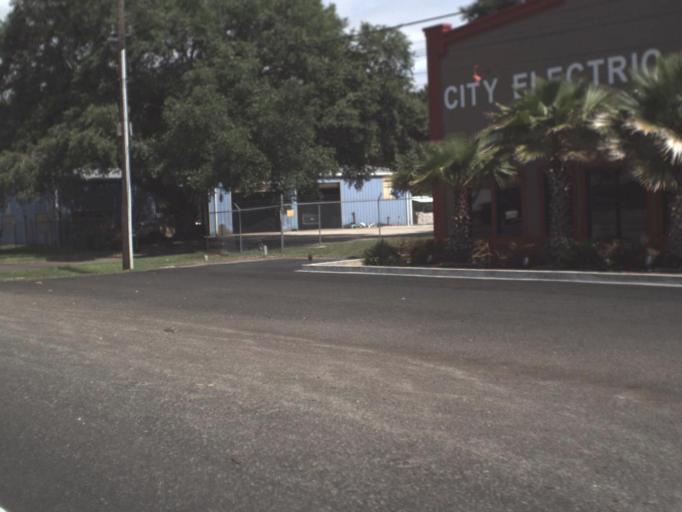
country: US
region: Florida
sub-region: Nassau County
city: Fernandina Beach
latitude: 30.6166
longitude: -81.5109
